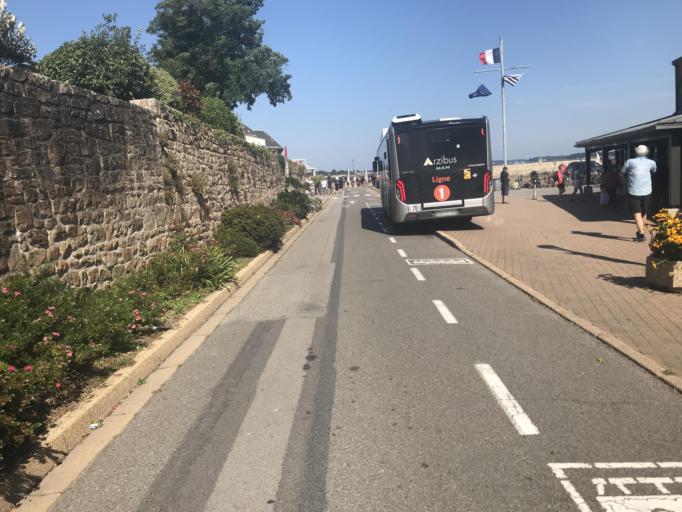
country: FR
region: Brittany
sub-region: Departement du Morbihan
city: Arzon
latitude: 47.5482
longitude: -2.9162
